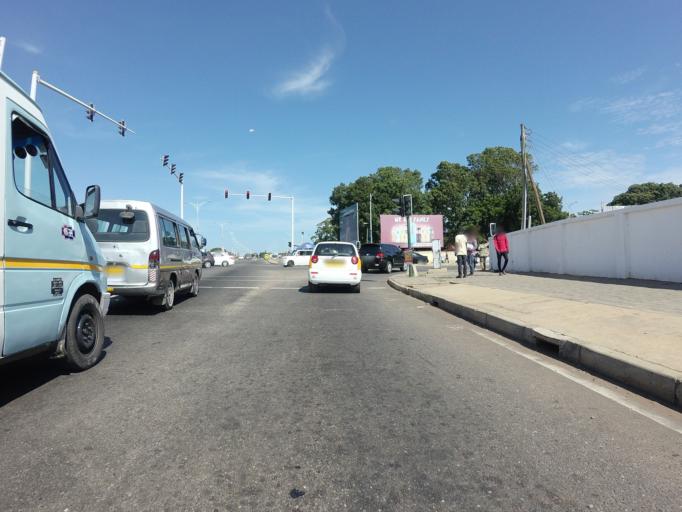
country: GH
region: Greater Accra
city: Accra
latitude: 5.5877
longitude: -0.1761
